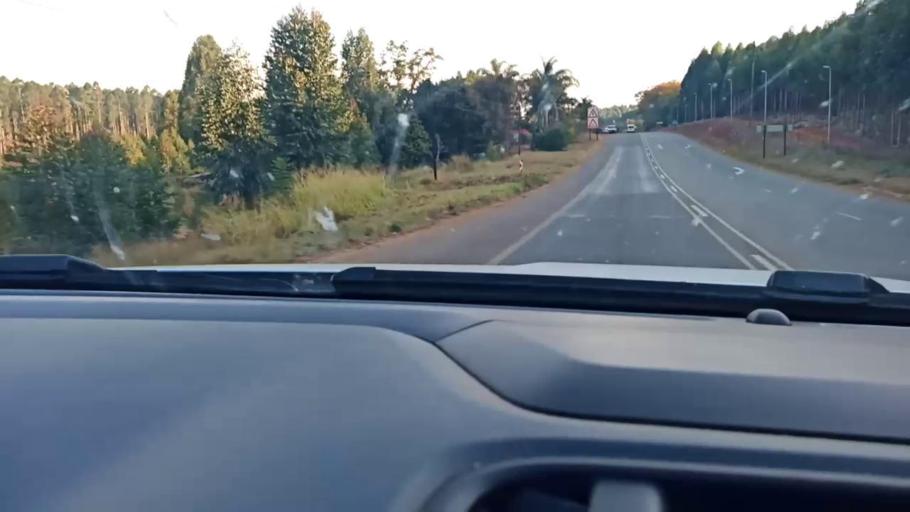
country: ZA
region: Limpopo
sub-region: Mopani District Municipality
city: Duiwelskloof
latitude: -23.7014
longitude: 30.1353
